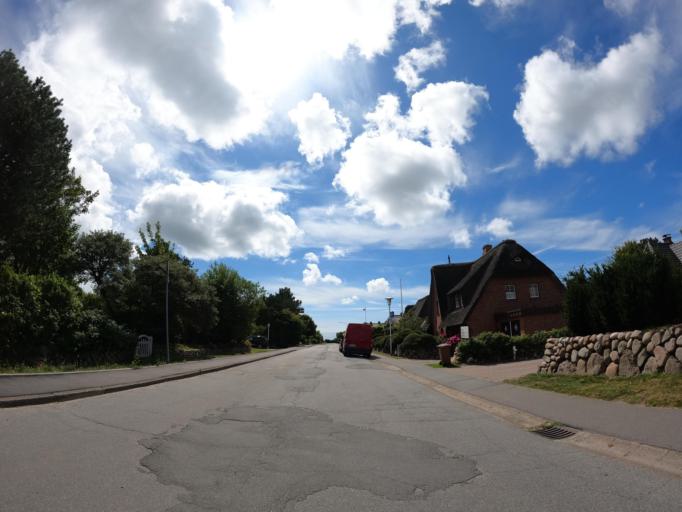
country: DE
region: Schleswig-Holstein
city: Keitum
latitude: 54.8931
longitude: 8.3640
